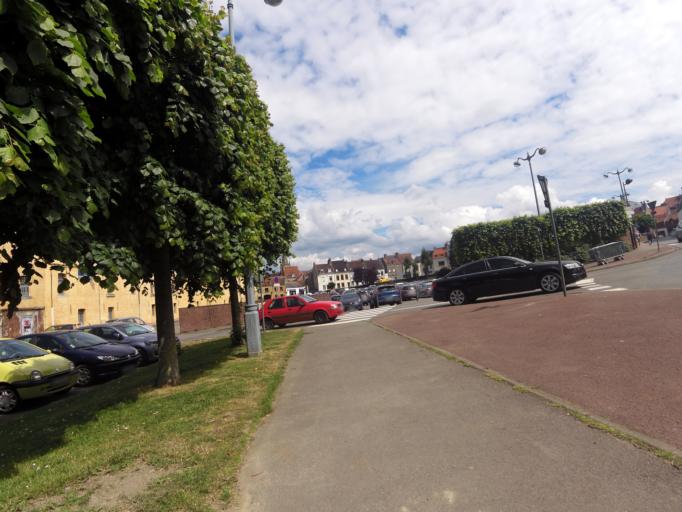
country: FR
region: Nord-Pas-de-Calais
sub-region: Departement du Pas-de-Calais
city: Saint-Omer
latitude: 50.7520
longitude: 2.2491
